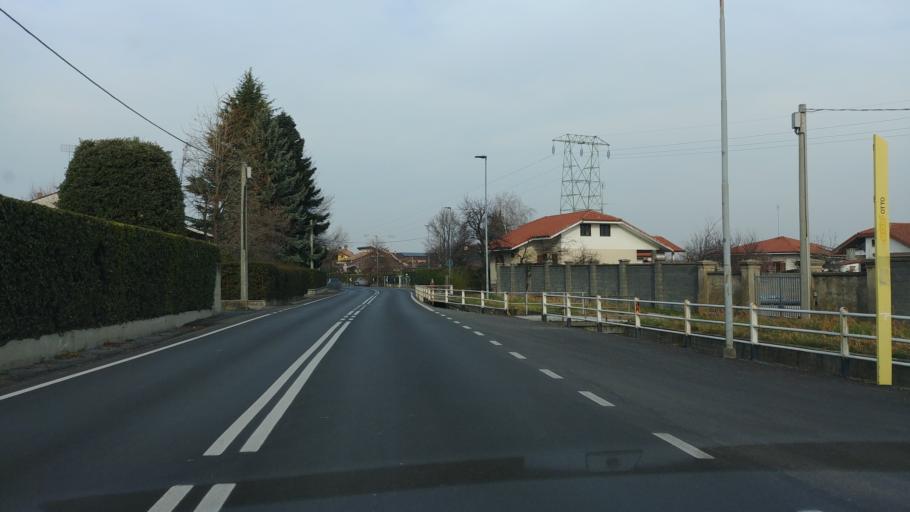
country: IT
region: Piedmont
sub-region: Provincia di Cuneo
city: Borgo San Dalmazzo
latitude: 44.3491
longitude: 7.5132
